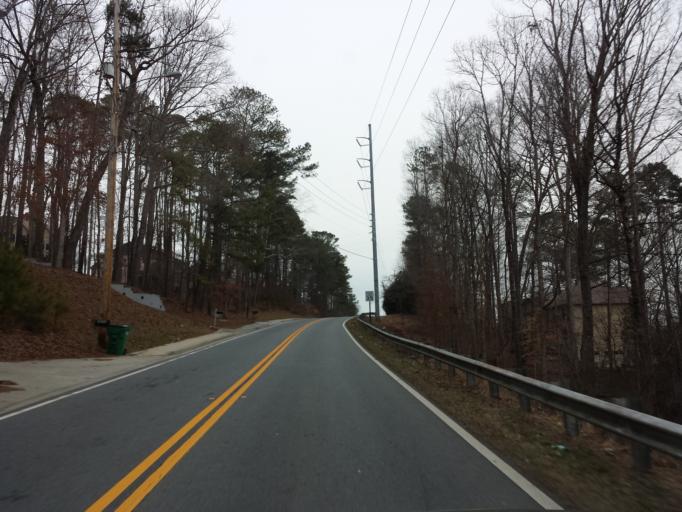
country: US
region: Georgia
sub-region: Fulton County
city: Roswell
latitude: 34.0185
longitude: -84.4070
